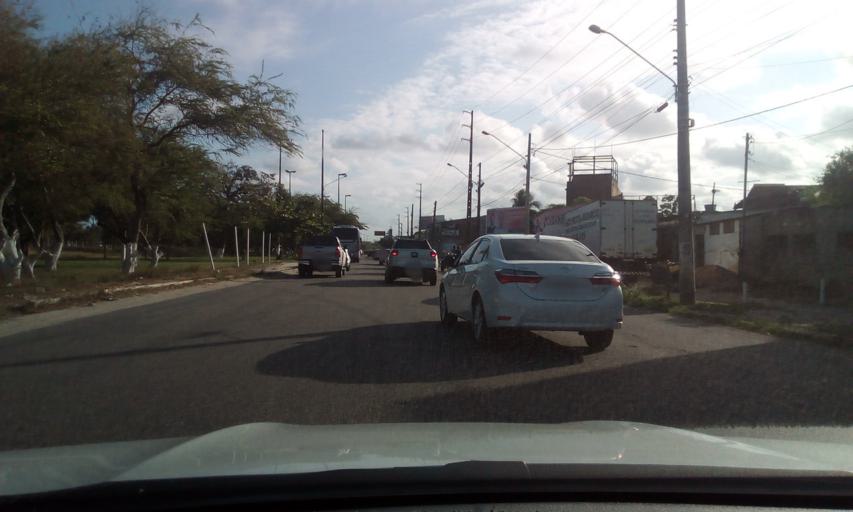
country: BR
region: Pernambuco
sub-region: Olinda
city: Olinda
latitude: -8.0285
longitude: -34.8658
